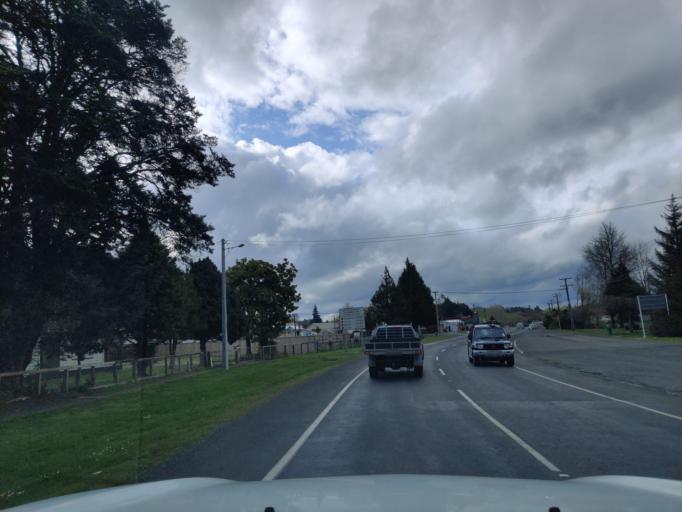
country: NZ
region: Manawatu-Wanganui
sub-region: Ruapehu District
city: Waiouru
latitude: -39.4299
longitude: 175.2818
